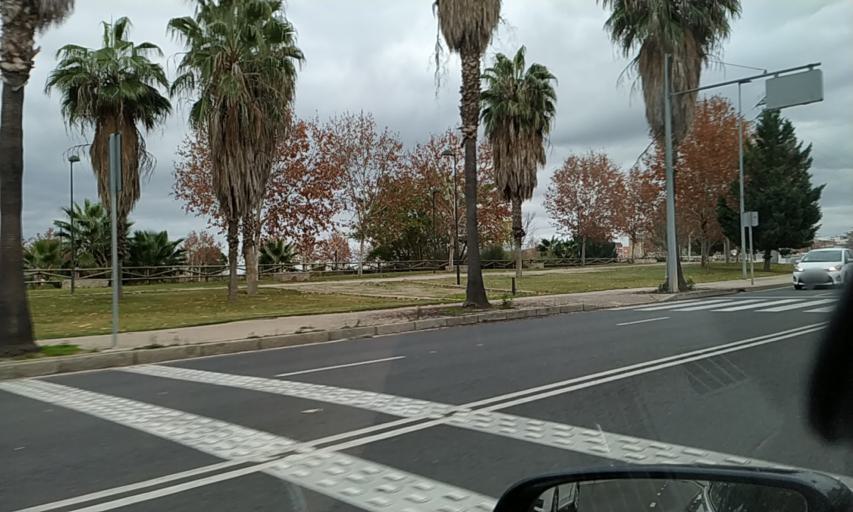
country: ES
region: Extremadura
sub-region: Provincia de Badajoz
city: Badajoz
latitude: 38.8833
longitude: -6.9657
